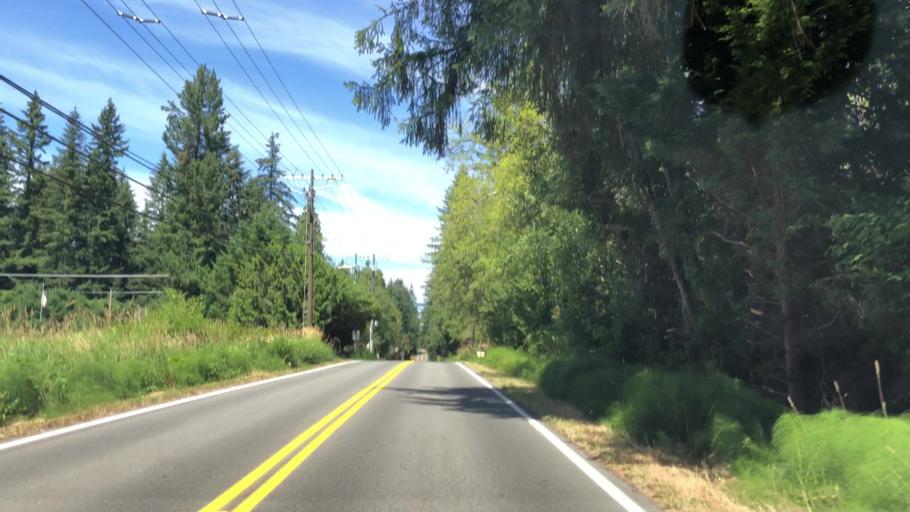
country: US
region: Washington
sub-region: Snohomish County
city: North Creek
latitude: 47.8330
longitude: -122.1641
